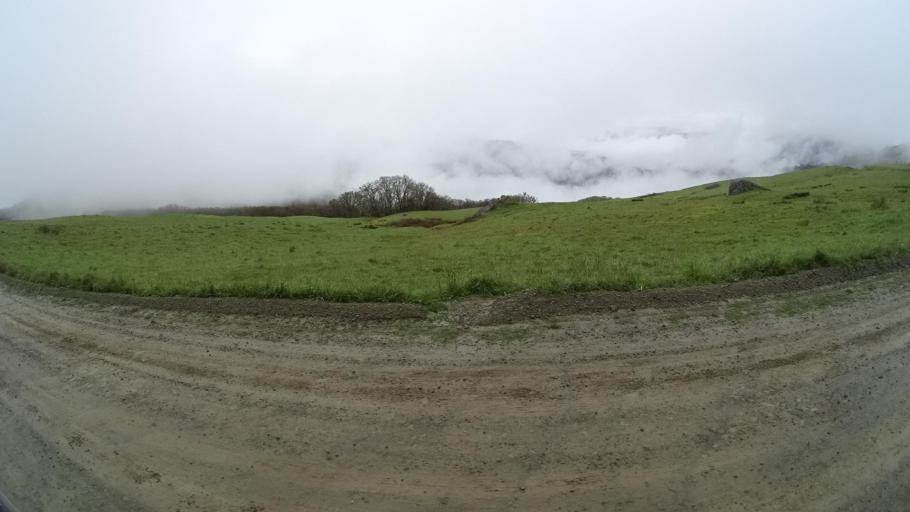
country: US
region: California
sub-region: Humboldt County
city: Westhaven-Moonstone
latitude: 41.1482
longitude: -123.8764
